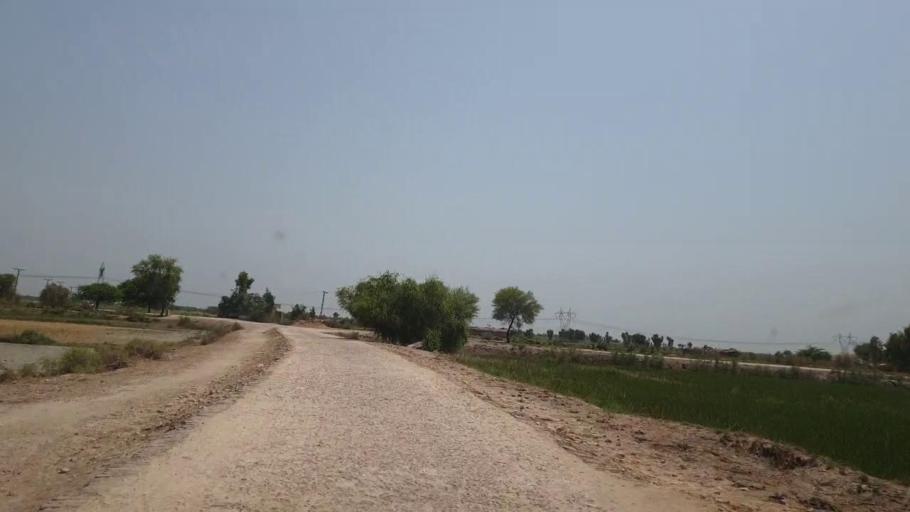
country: PK
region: Sindh
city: Garhi Yasin
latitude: 27.8486
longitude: 68.5875
